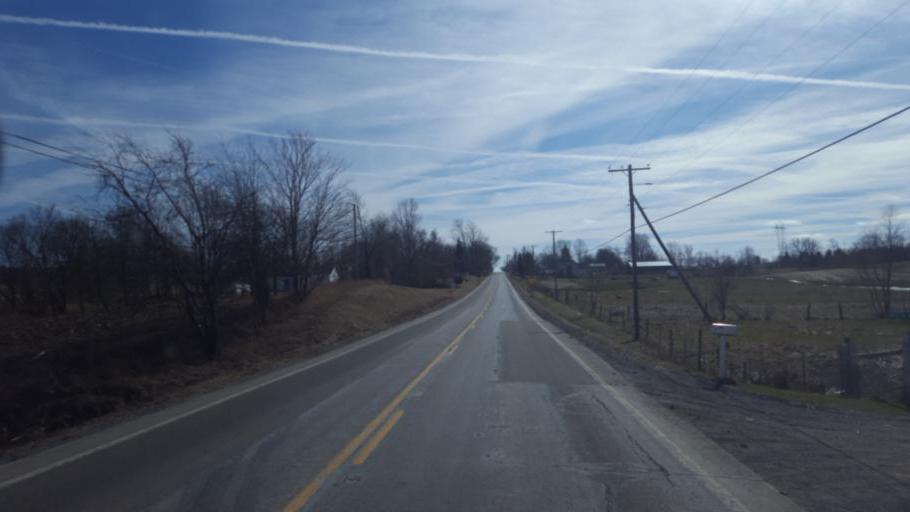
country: US
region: Ohio
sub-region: Richland County
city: Lexington
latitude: 40.5998
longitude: -82.6624
